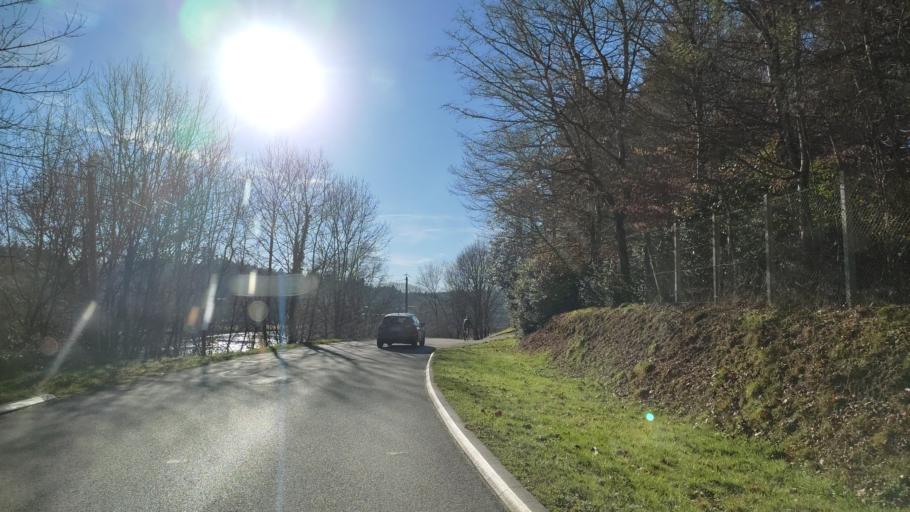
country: FR
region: Limousin
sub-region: Departement de la Haute-Vienne
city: Isle
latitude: 45.7861
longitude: 1.2095
